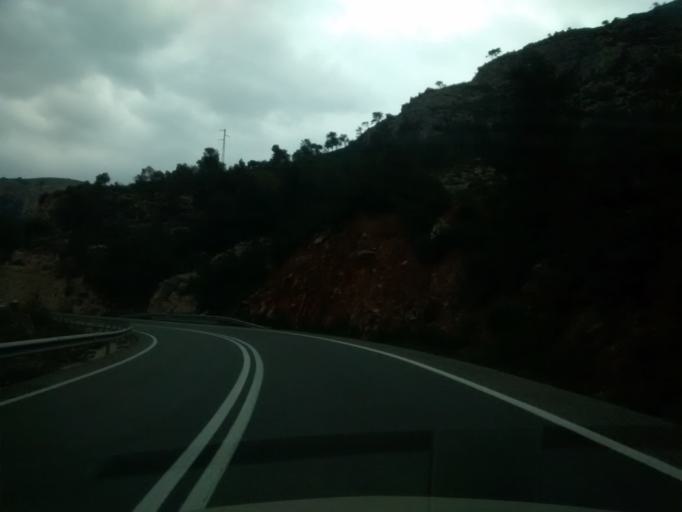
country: ES
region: Catalonia
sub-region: Provincia de Tarragona
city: Gandesa
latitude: 41.0338
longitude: 0.4926
